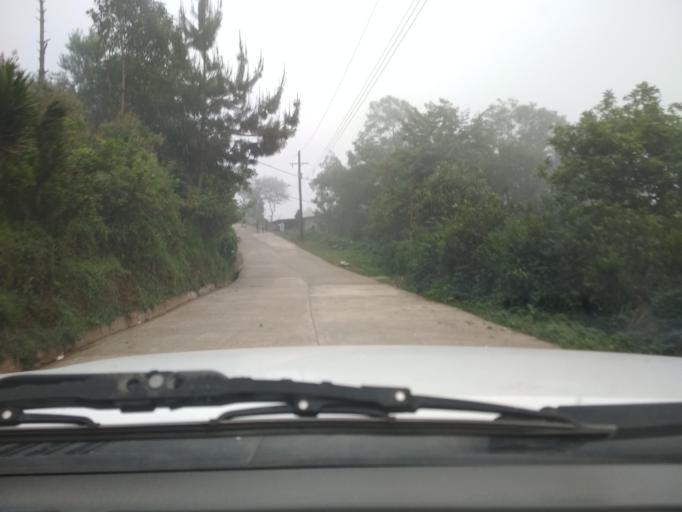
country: MX
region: Veracruz
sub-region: La Perla
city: Barrio de San Miguel
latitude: 18.9509
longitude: -97.1234
